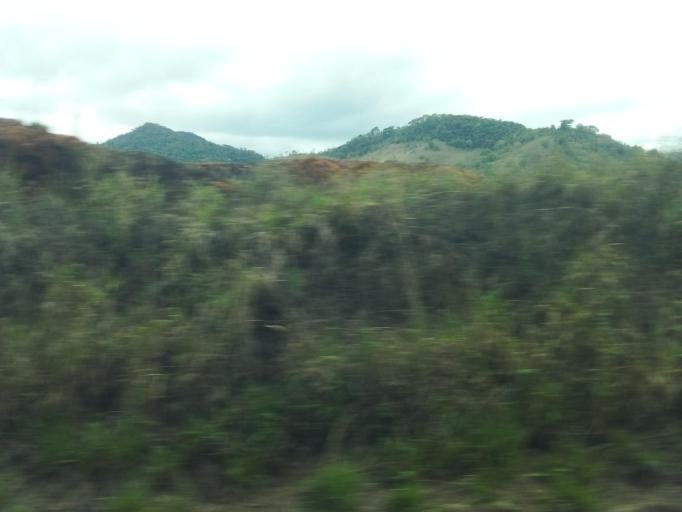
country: BR
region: Minas Gerais
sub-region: Nova Era
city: Nova Era
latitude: -19.6840
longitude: -42.9096
